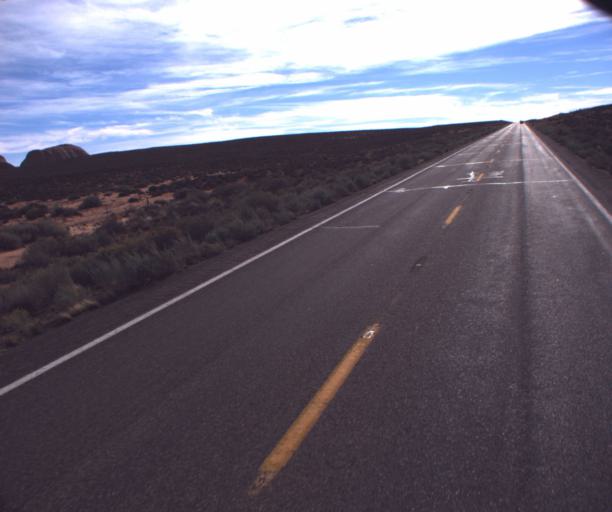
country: US
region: Arizona
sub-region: Coconino County
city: LeChee
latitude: 36.8371
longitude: -111.3211
